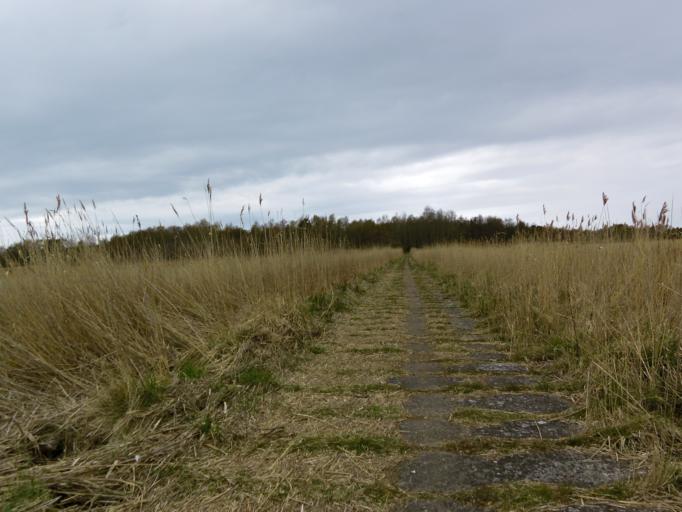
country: DE
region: Mecklenburg-Vorpommern
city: Hiddensee
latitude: 54.5460
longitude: 13.1111
